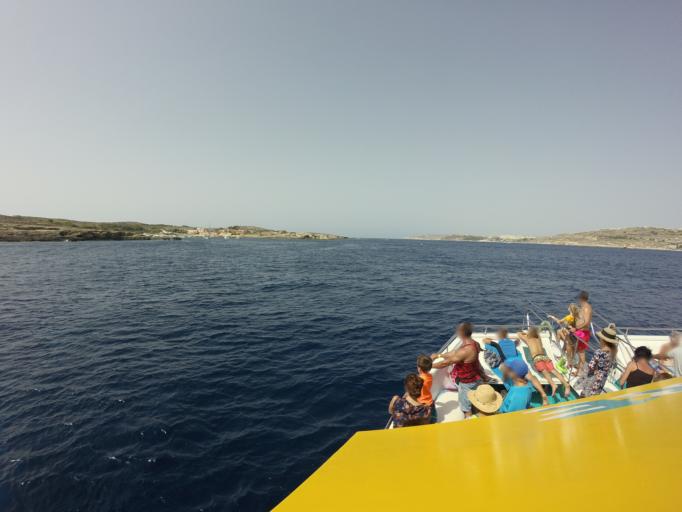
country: MT
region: Il-Qala
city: Qala
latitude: 36.0213
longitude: 14.3331
